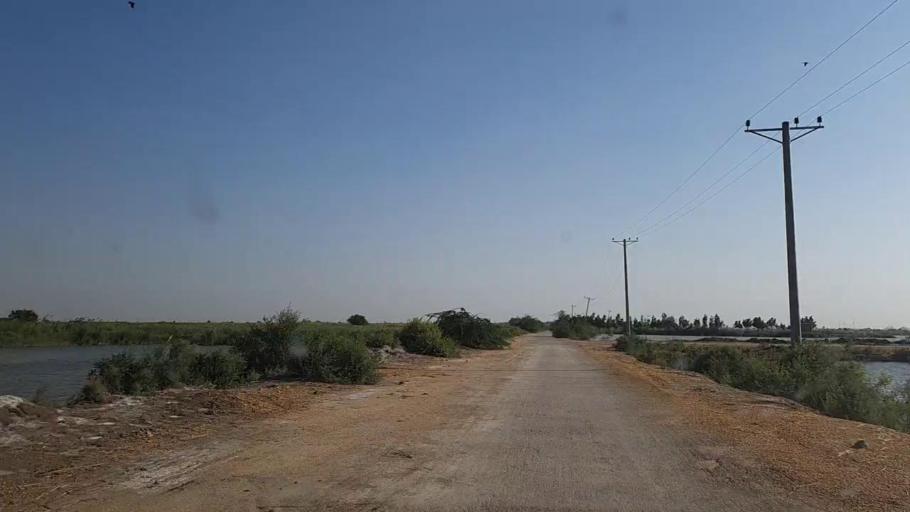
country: PK
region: Sindh
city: Thatta
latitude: 24.6405
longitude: 68.0755
